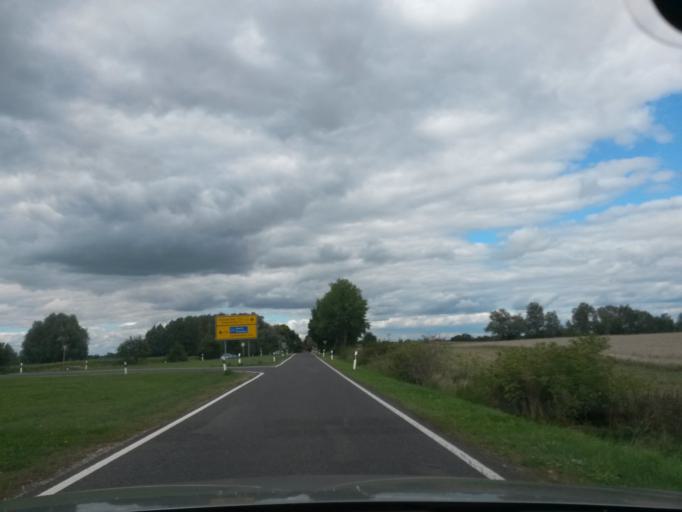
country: DE
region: Brandenburg
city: Angermunde
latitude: 52.9699
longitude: 13.9652
